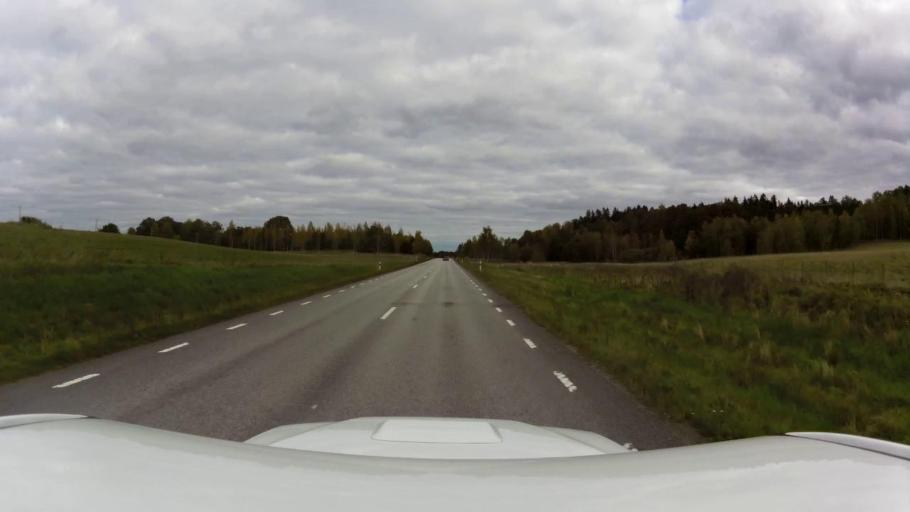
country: SE
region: OEstergoetland
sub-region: Kinda Kommun
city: Rimforsa
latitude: 58.2021
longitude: 15.6682
